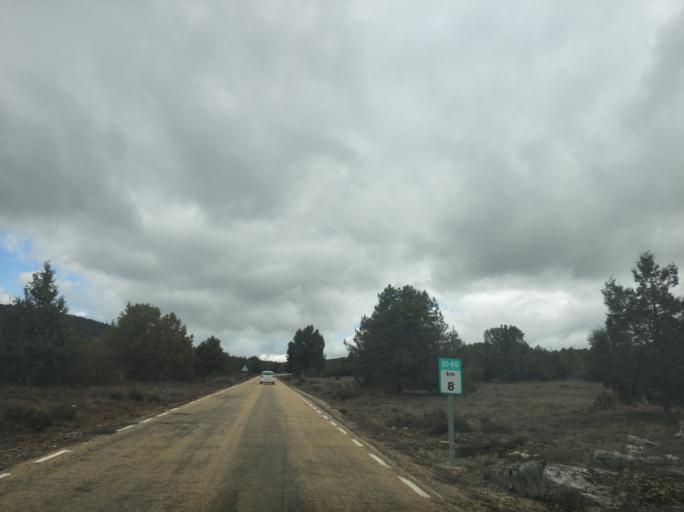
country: ES
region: Castille and Leon
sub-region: Provincia de Soria
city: Abejar
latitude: 41.7772
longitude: -2.7770
